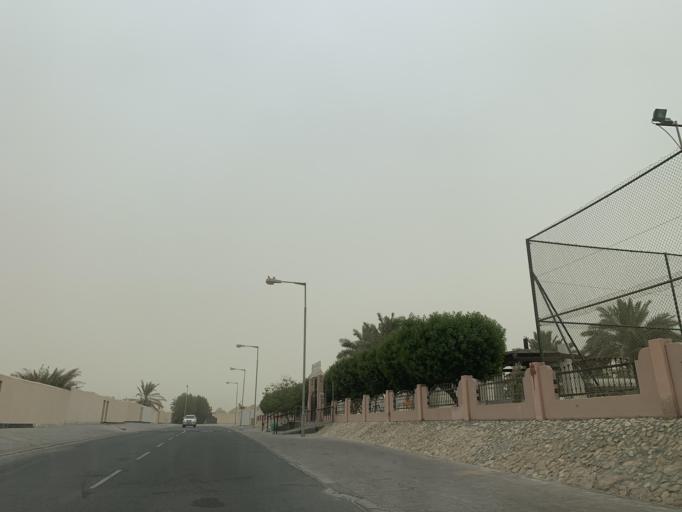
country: BH
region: Central Governorate
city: Madinat Hamad
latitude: 26.1329
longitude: 50.5235
